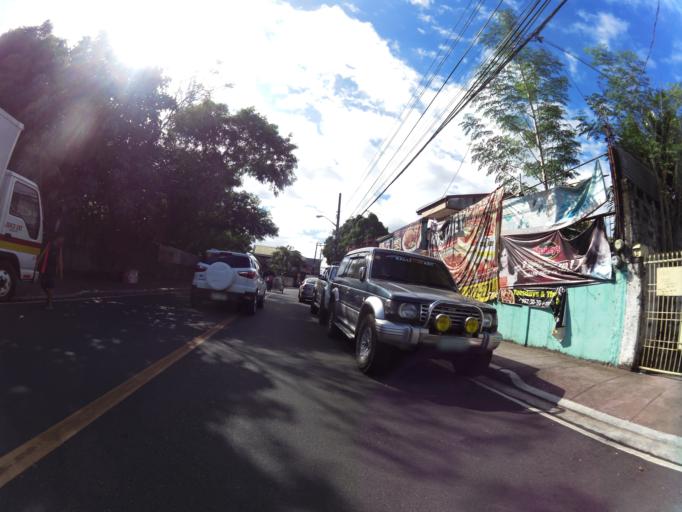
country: PH
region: Metro Manila
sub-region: Marikina
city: Calumpang
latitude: 14.6271
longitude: 121.0998
